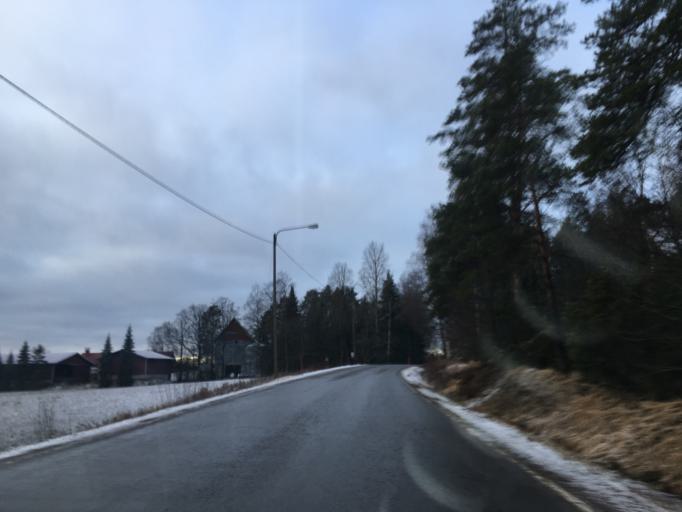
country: FI
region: Varsinais-Suomi
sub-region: Loimaa
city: Aura
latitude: 60.5858
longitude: 22.5192
